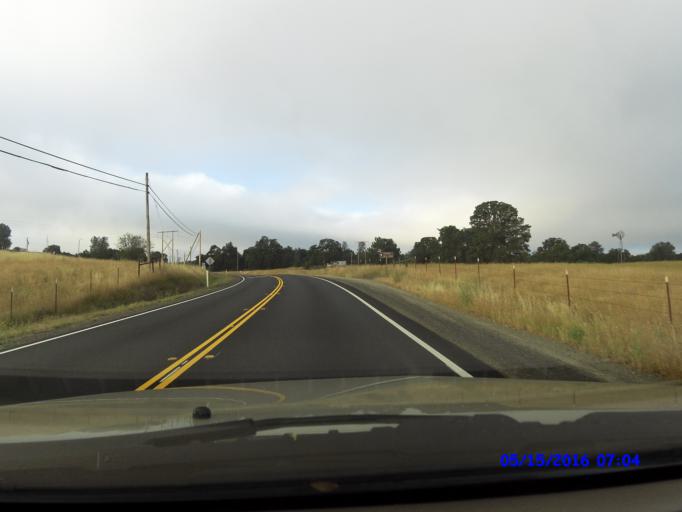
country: US
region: California
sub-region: Tuolumne County
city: Jamestown
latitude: 37.9176
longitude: -120.4522
